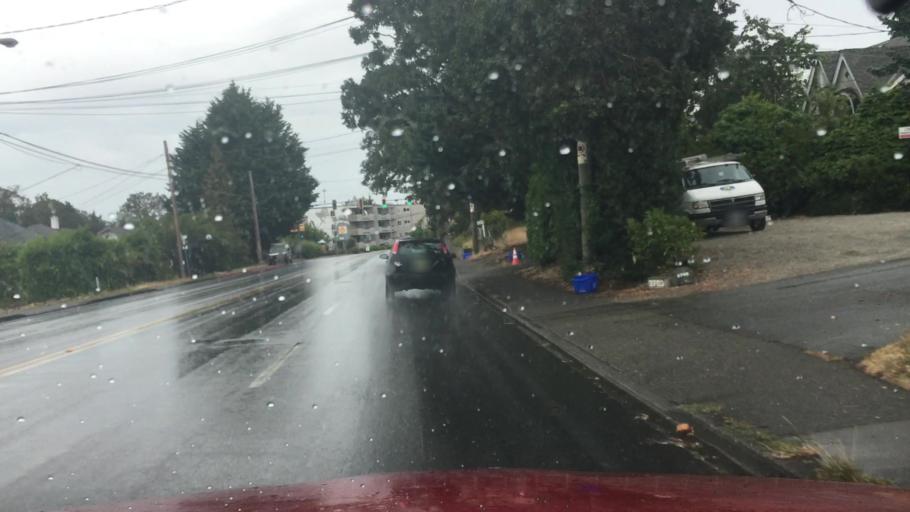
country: CA
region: British Columbia
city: Victoria
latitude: 48.4596
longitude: -123.3603
